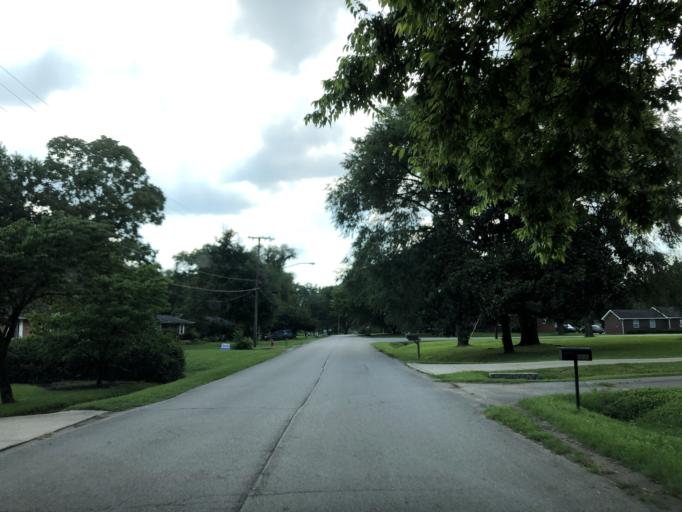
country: US
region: Tennessee
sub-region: Davidson County
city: Oak Hill
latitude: 36.1190
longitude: -86.7210
